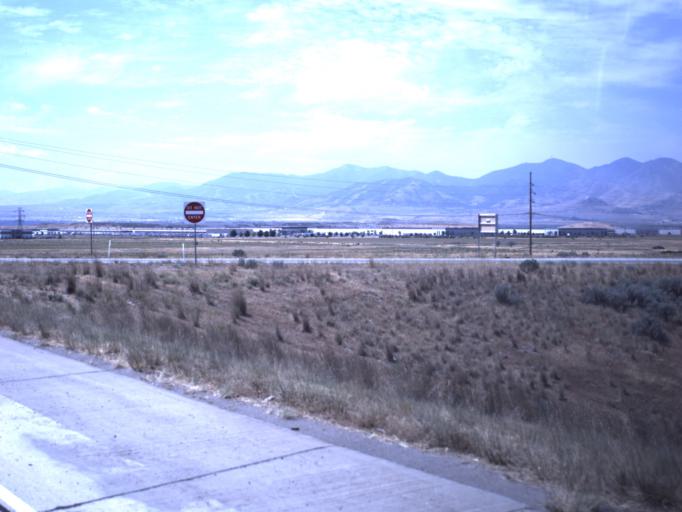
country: US
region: Utah
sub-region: Salt Lake County
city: West Valley City
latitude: 40.7696
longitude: -112.0252
